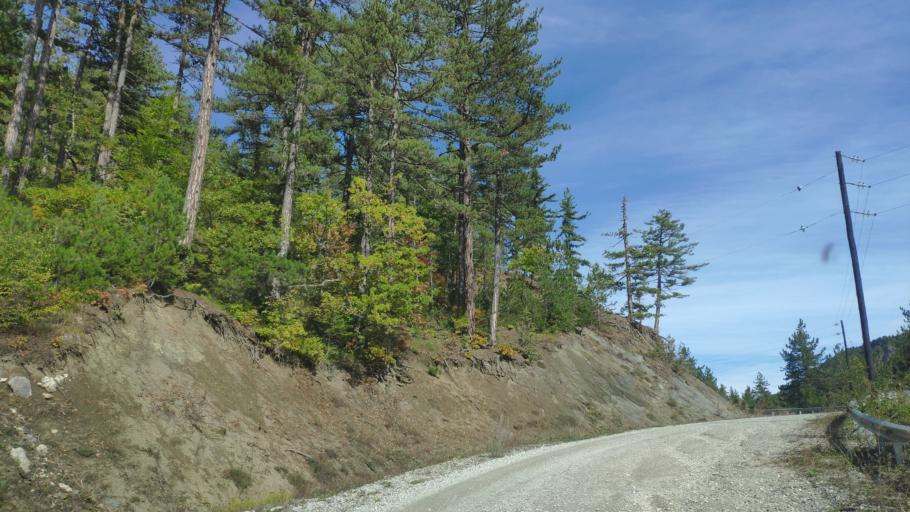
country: AL
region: Korce
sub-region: Rrethi i Devollit
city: Miras
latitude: 40.4155
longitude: 20.8706
